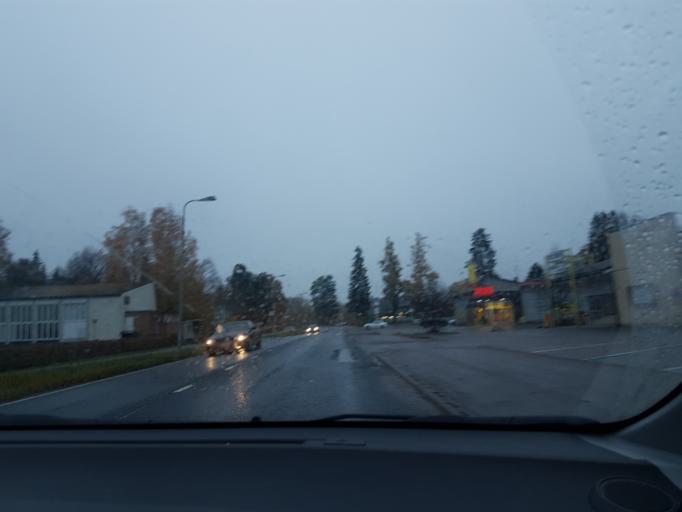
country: FI
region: Uusimaa
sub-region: Helsinki
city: Jaervenpaeae
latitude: 60.5311
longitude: 25.1092
